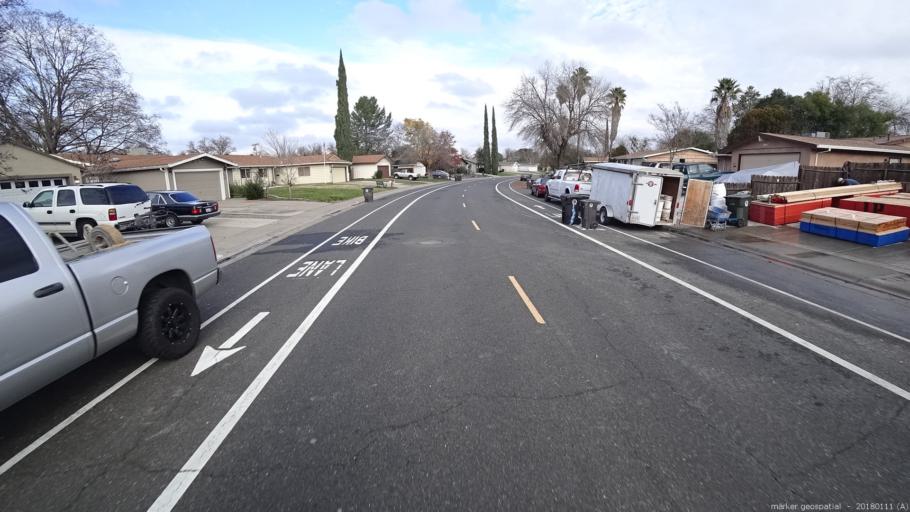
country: US
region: California
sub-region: Sacramento County
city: Rancho Cordova
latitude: 38.6130
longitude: -121.2988
